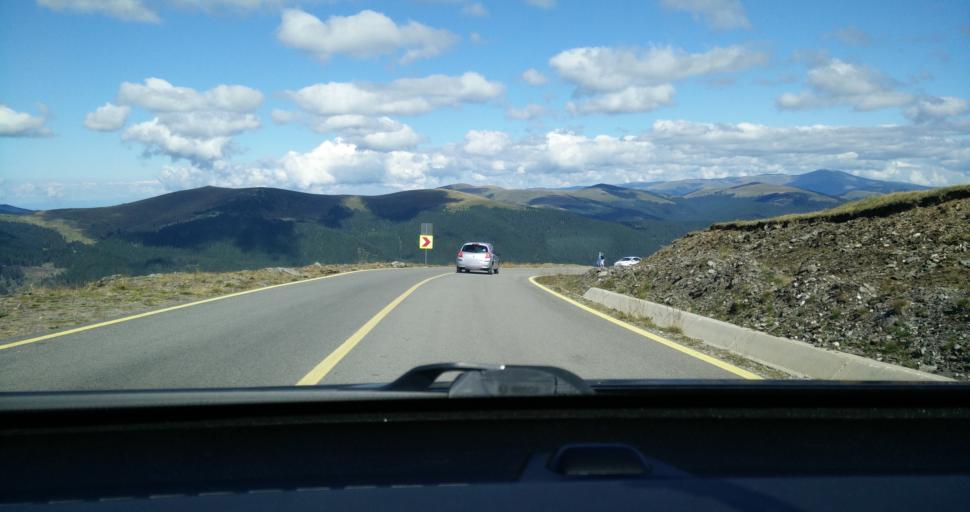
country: RO
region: Gorj
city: Novaci-Straini
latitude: 45.3771
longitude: 23.6526
